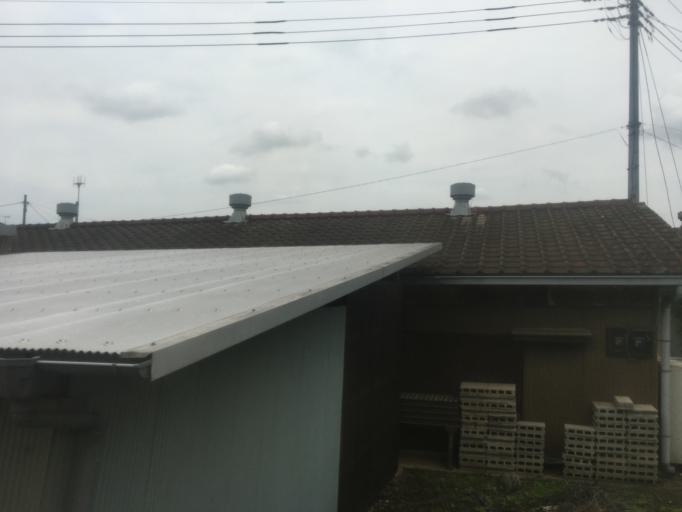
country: JP
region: Gunma
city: Tomioka
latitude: 36.2599
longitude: 138.8767
